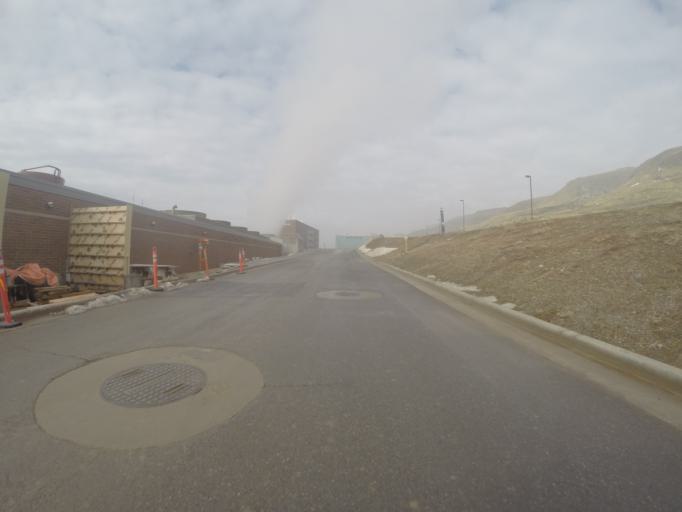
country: US
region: Utah
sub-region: Salt Lake County
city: Salt Lake City
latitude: 40.7686
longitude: -111.8300
